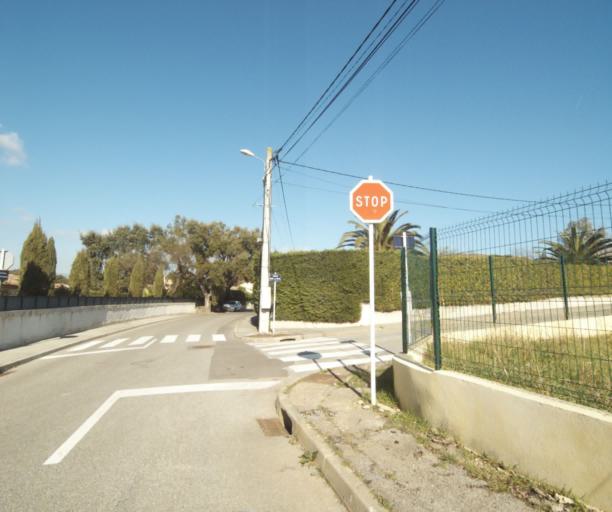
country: FR
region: Provence-Alpes-Cote d'Azur
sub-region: Departement des Alpes-Maritimes
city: Biot
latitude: 43.6199
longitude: 7.1189
